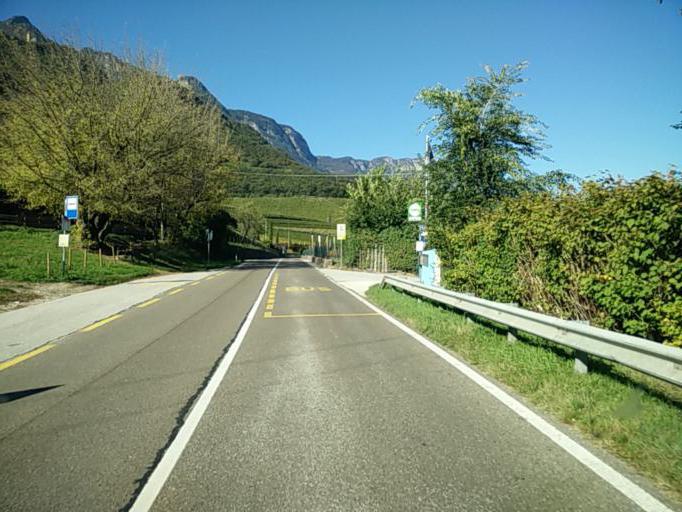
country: IT
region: Trentino-Alto Adige
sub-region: Bolzano
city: Termeno
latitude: 46.3722
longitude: 11.2522
